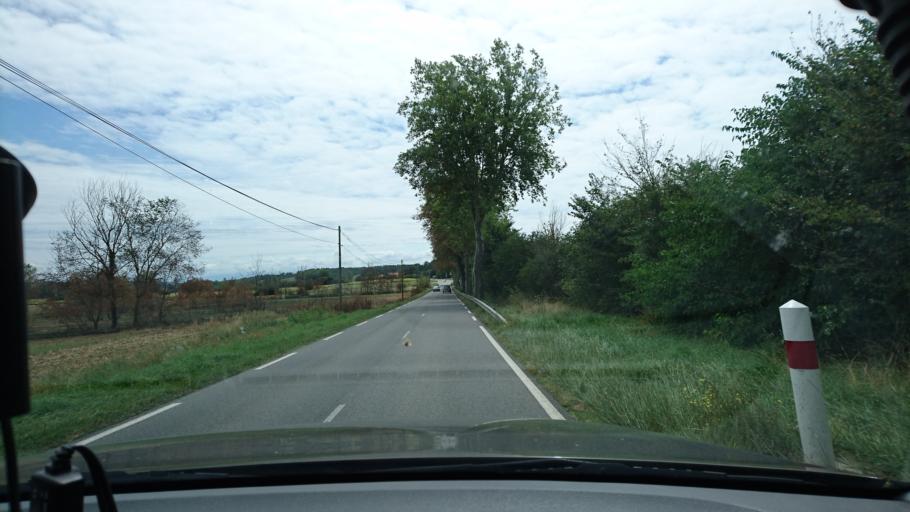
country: FR
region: Midi-Pyrenees
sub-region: Departement de la Haute-Garonne
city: Saint-Sulpice-sur-Leze
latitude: 43.3190
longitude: 1.3230
